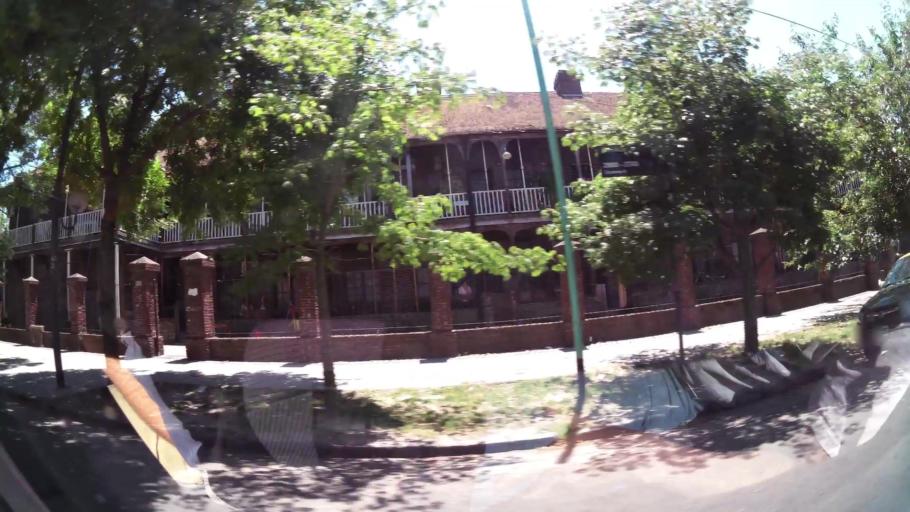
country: AR
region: Buenos Aires
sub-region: Partido de Avellaneda
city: Avellaneda
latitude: -34.6466
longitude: -58.3862
